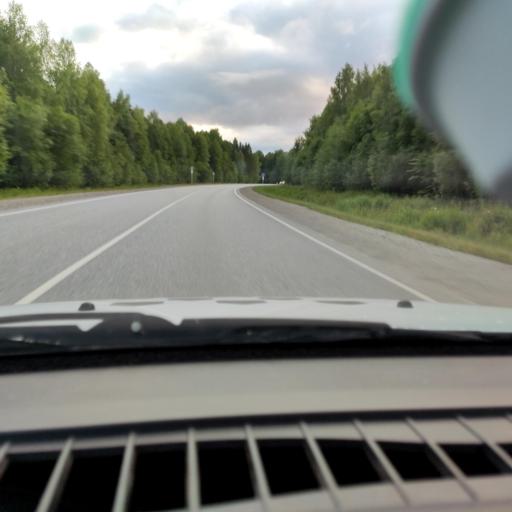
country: RU
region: Perm
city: Polazna
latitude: 58.2993
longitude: 56.5615
